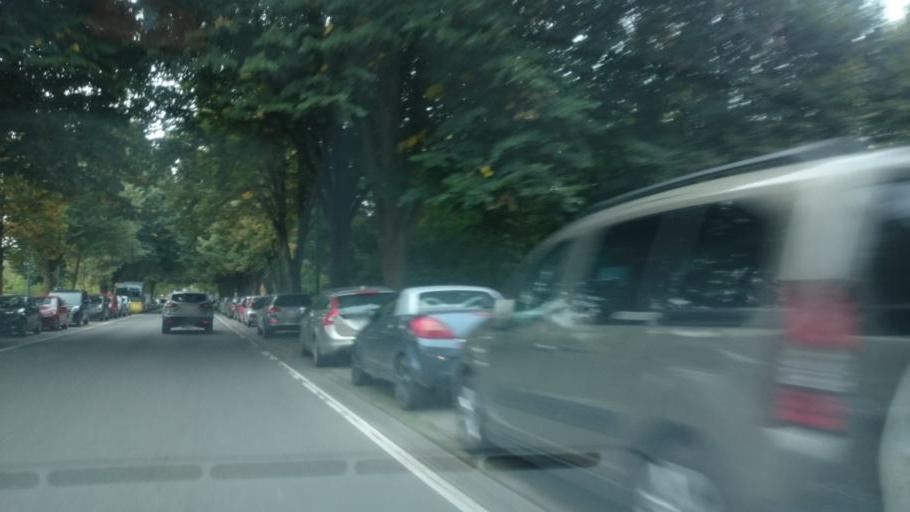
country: BE
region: Wallonia
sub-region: Province de Namur
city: Namur
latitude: 50.4639
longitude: 4.8396
